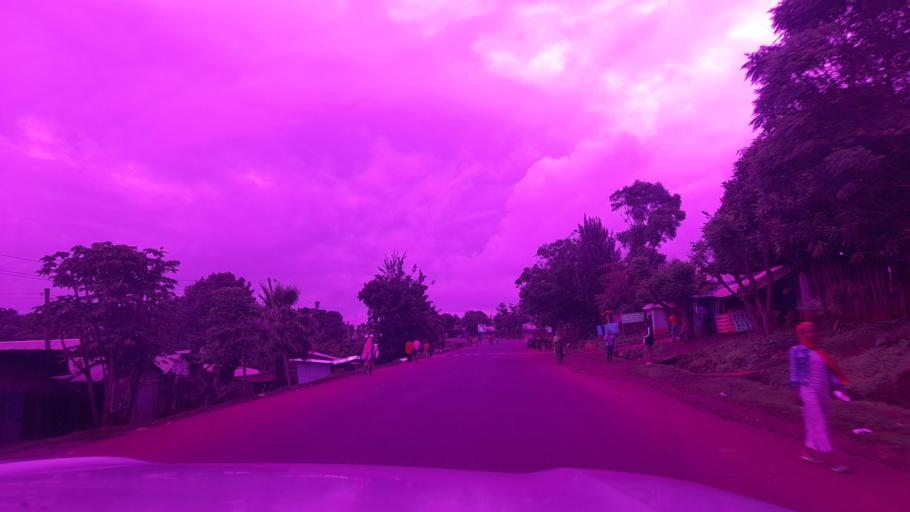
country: ET
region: Oromiya
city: Jima
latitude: 7.9662
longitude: 37.4405
